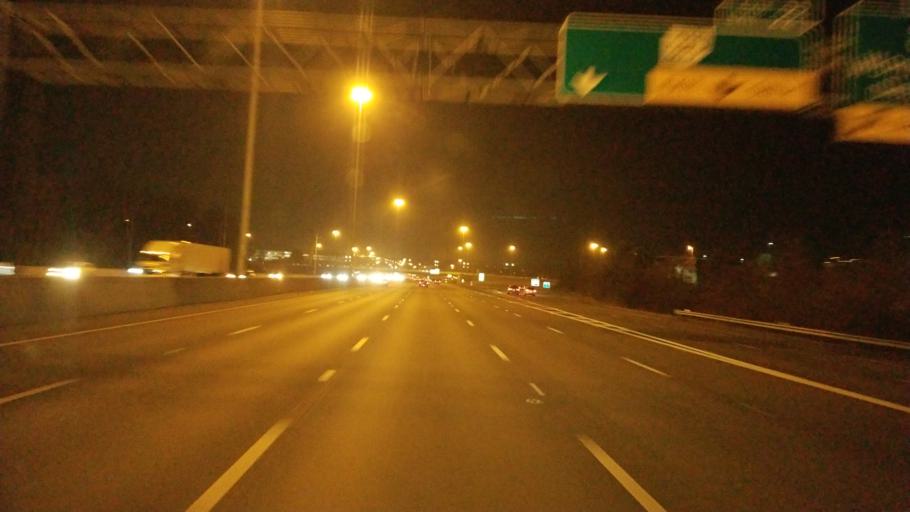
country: US
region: Ohio
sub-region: Franklin County
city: Worthington
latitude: 40.1121
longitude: -83.0092
